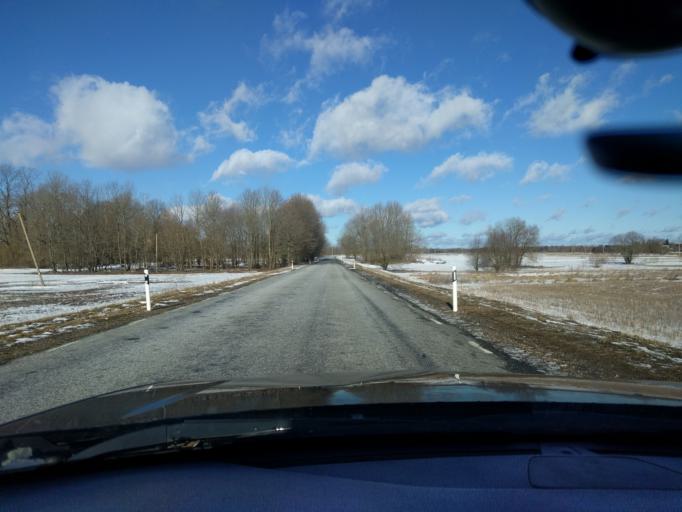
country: EE
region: Harju
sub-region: Raasiku vald
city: Raasiku
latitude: 59.3455
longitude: 25.1495
